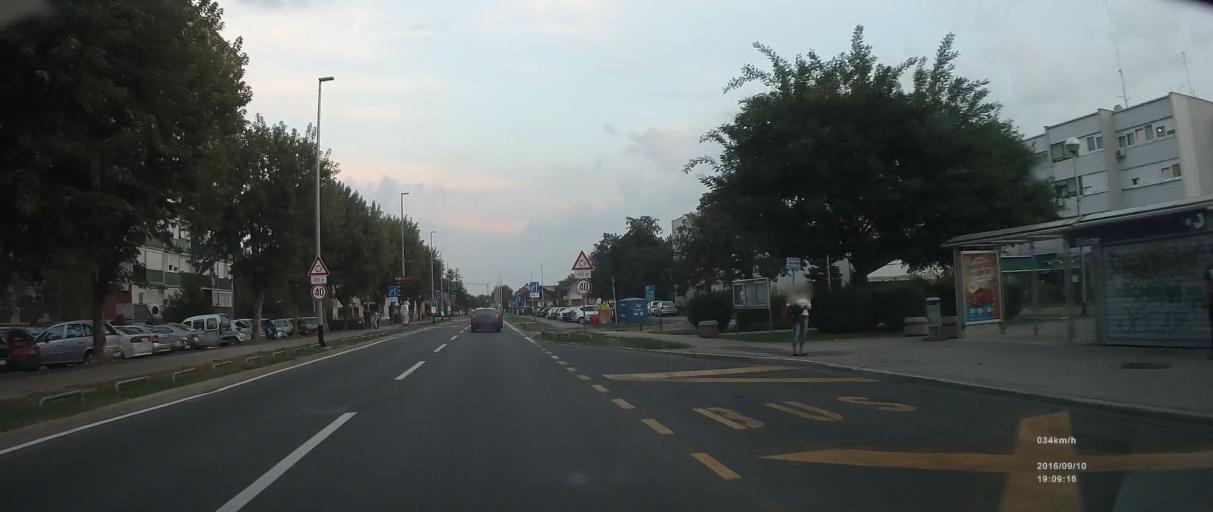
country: HR
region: Zagrebacka
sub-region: Grad Velika Gorica
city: Velika Gorica
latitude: 45.7128
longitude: 16.0675
